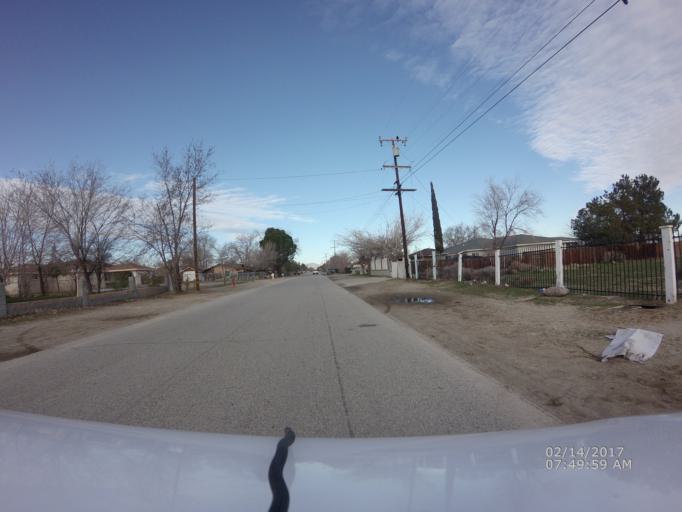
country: US
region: California
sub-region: Los Angeles County
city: Littlerock
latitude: 34.5502
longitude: -117.9470
